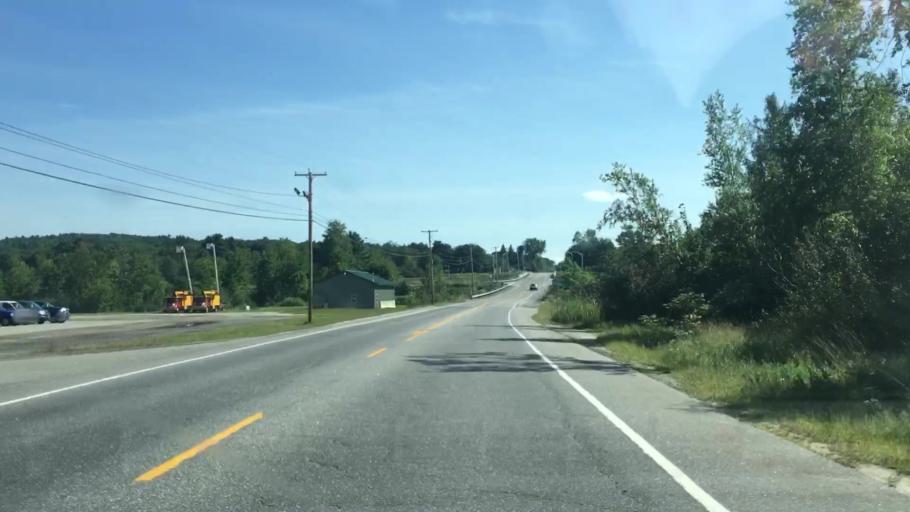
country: US
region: Maine
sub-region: Androscoggin County
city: Sabattus
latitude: 44.1044
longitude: -70.0873
